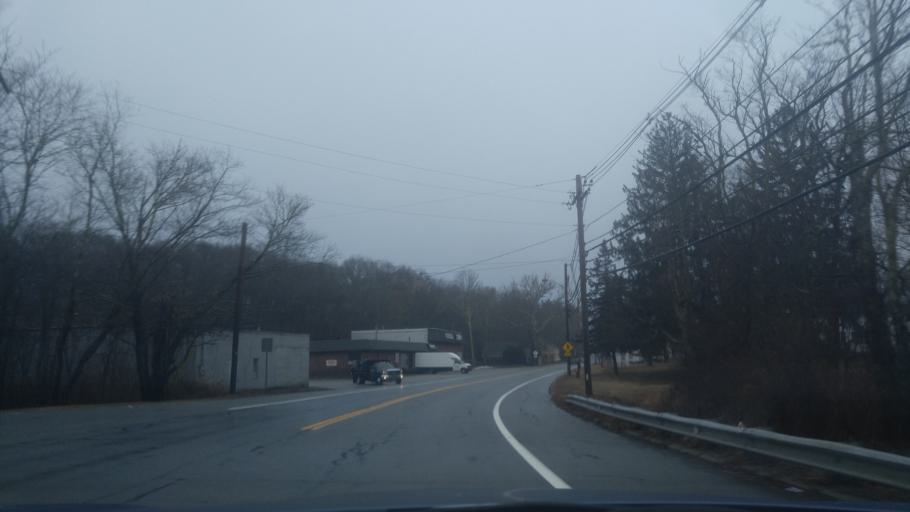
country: US
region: Rhode Island
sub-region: Washington County
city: North Kingstown
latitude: 41.5566
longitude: -71.4648
